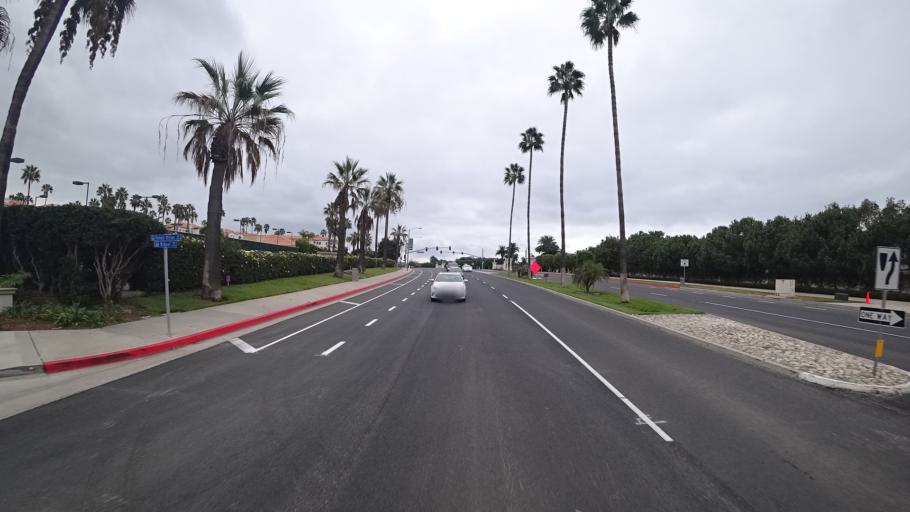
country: US
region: California
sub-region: Orange County
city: Dana Point
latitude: 33.4837
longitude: -117.7142
